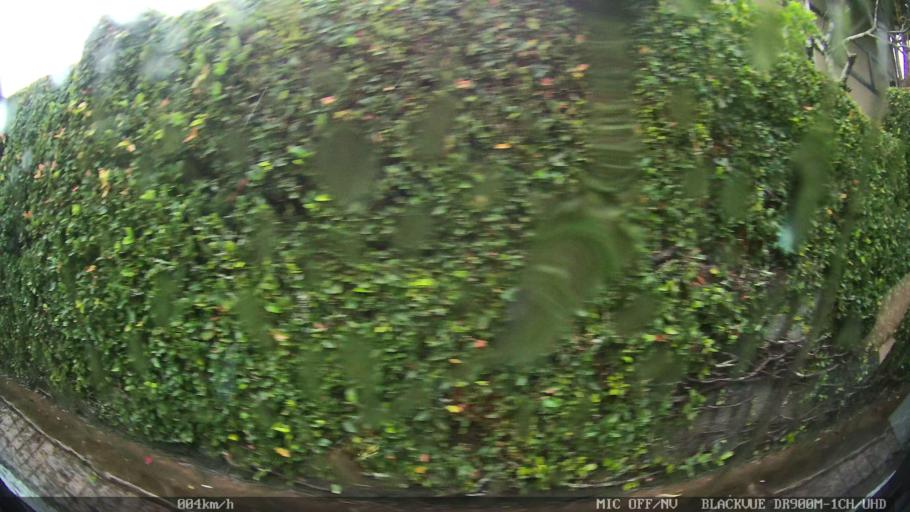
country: BR
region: Santa Catarina
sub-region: Itajai
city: Itajai
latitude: -26.9294
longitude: -48.6331
